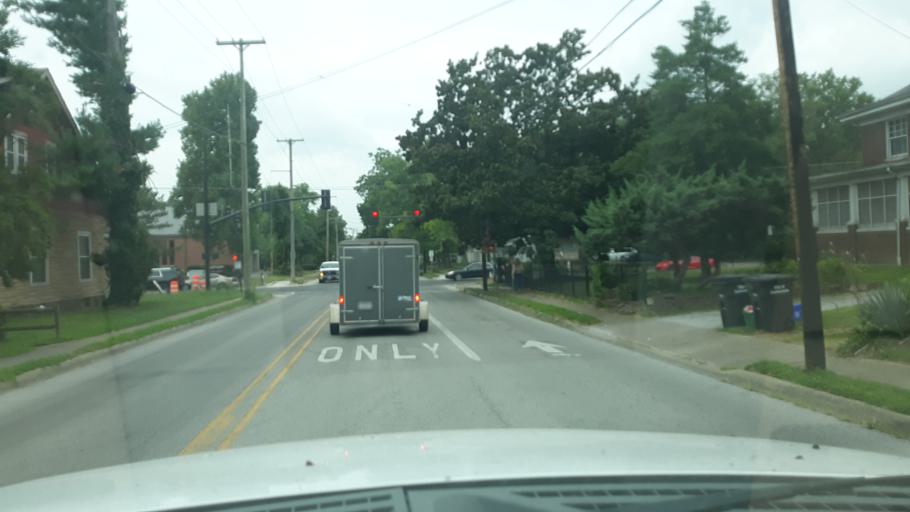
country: US
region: Illinois
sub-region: Jackson County
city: Carbondale
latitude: 37.7254
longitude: -89.2219
